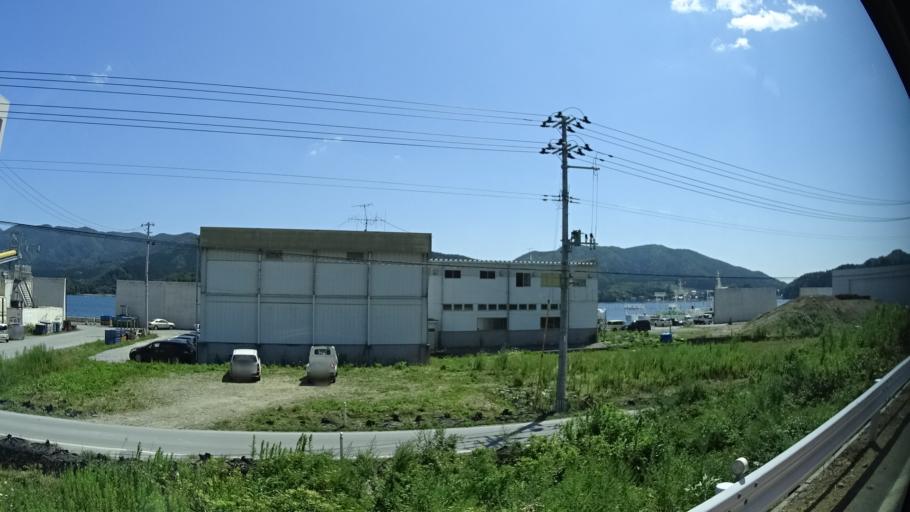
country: JP
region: Iwate
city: Ofunato
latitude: 39.0427
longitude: 141.7236
